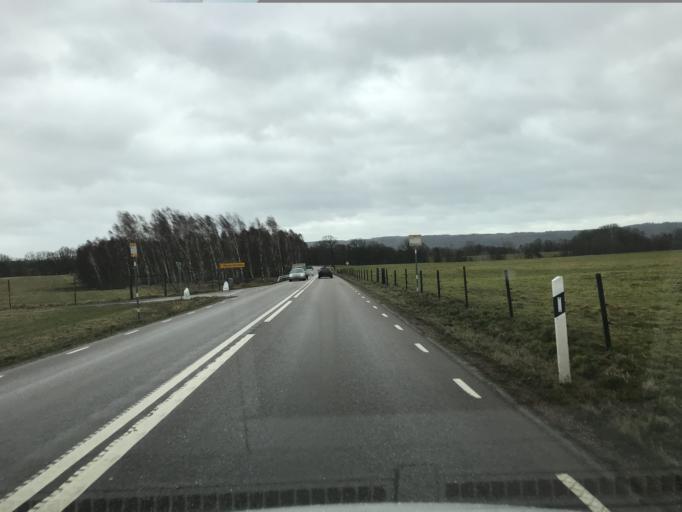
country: SE
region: Skane
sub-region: Klippans Kommun
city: Klippan
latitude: 56.1133
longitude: 13.1794
